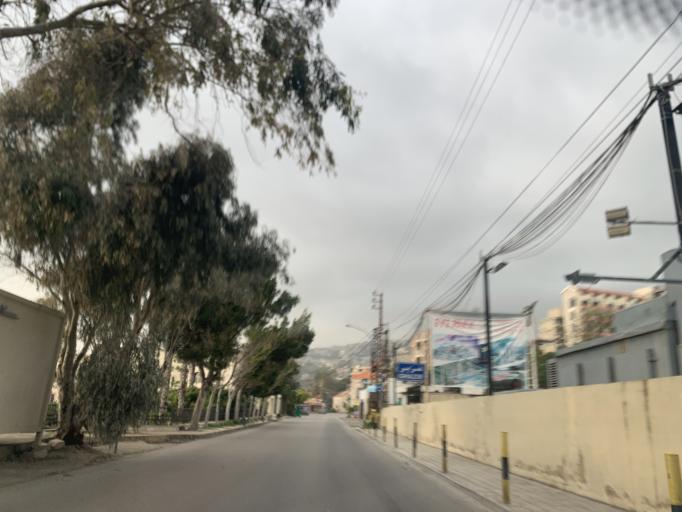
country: LB
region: Mont-Liban
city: Djounie
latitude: 34.0046
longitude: 35.6451
